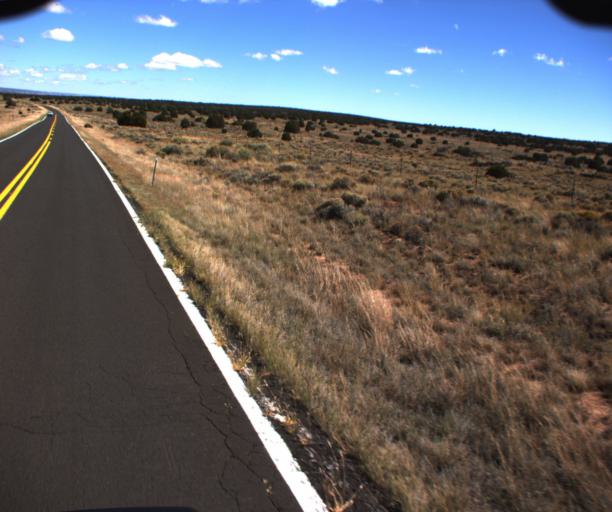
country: US
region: New Mexico
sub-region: McKinley County
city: Zuni Pueblo
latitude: 34.9920
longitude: -109.1034
